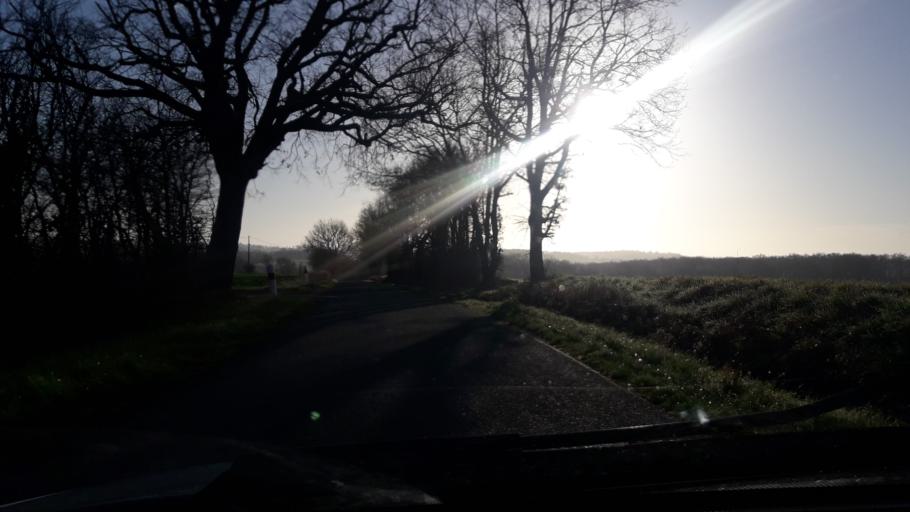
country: FR
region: Midi-Pyrenees
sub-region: Departement du Gers
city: Gimont
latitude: 43.6587
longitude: 0.9676
